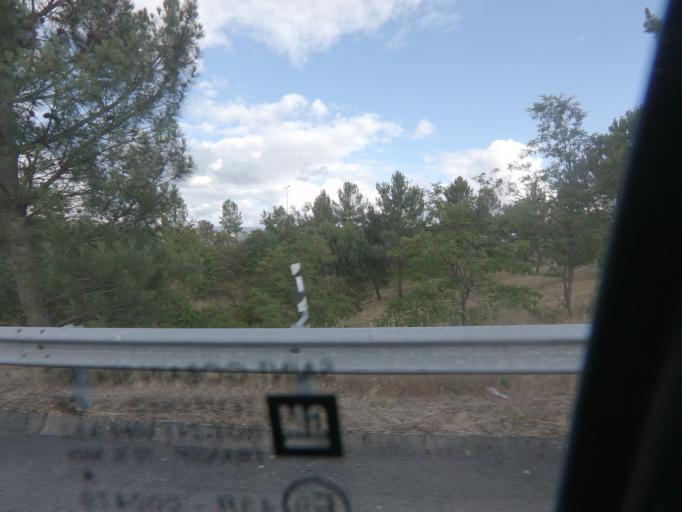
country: PT
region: Porto
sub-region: Marco de Canaveses
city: Marco de Canavezes
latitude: 41.2356
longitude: -8.1792
